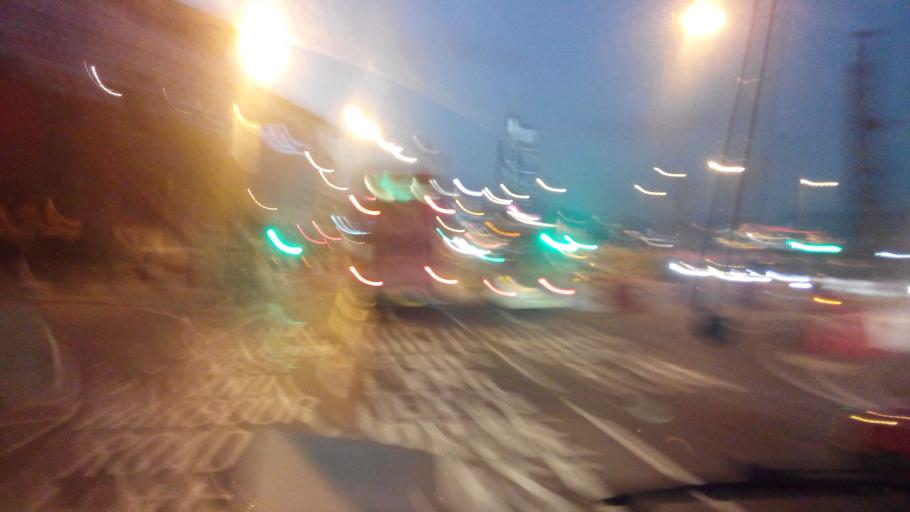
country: HK
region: Wanchai
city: Wan Chai
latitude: 22.2813
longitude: 114.1748
